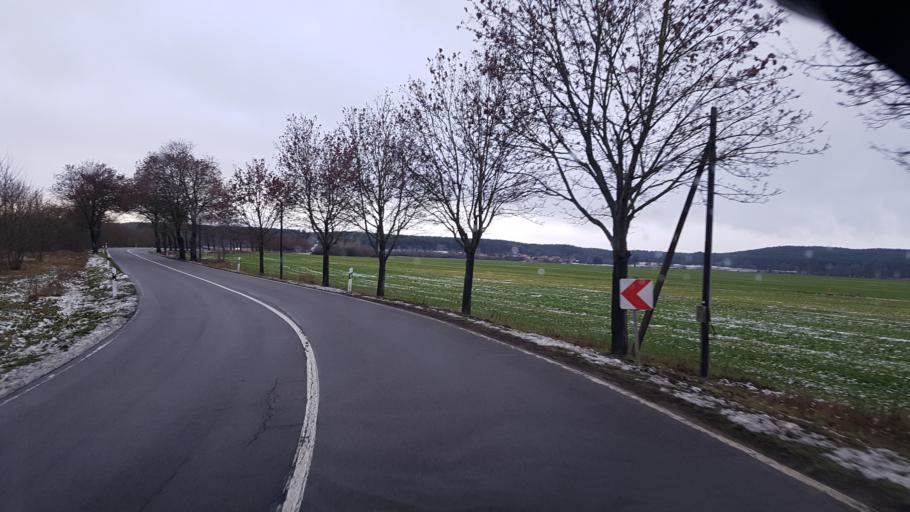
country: DE
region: Brandenburg
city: Schenkendobern
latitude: 51.8814
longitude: 14.6396
